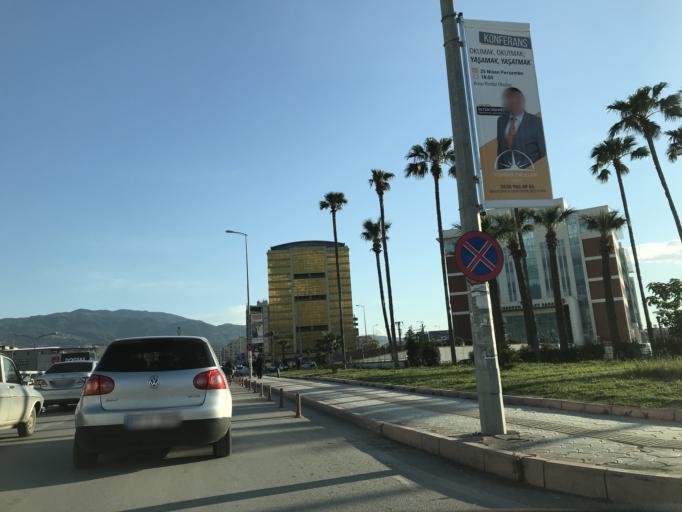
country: TR
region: Hatay
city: Iskenderun
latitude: 36.5753
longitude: 36.1606
